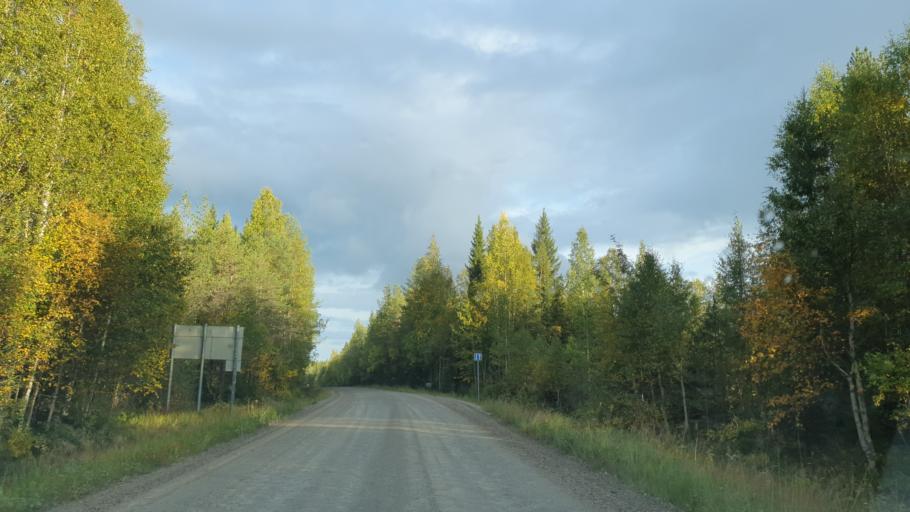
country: FI
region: Kainuu
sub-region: Kehys-Kainuu
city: Kuhmo
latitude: 64.4286
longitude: 29.3259
